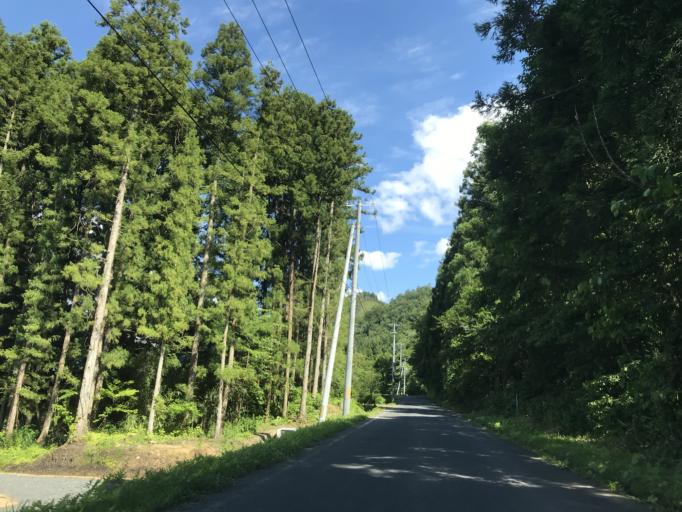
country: JP
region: Iwate
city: Ichinoseki
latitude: 38.9692
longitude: 140.9492
